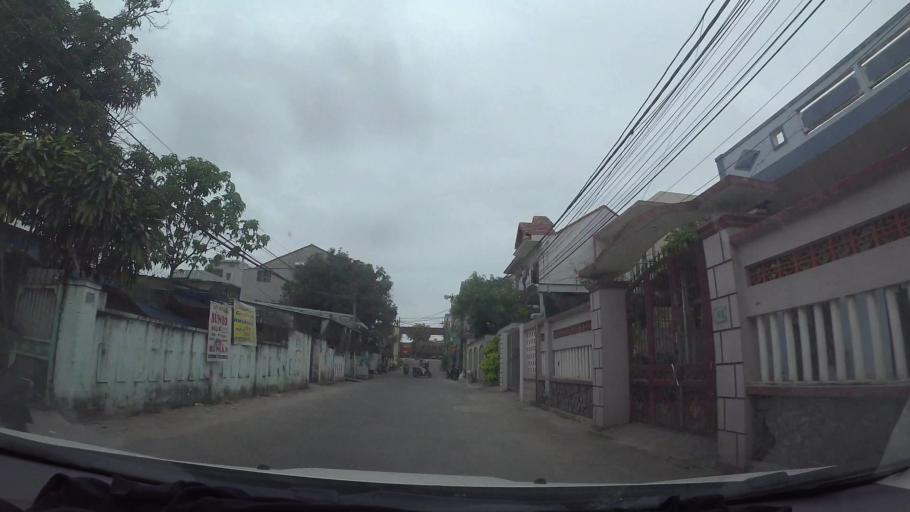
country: VN
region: Da Nang
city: Lien Chieu
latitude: 16.0858
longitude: 108.1441
